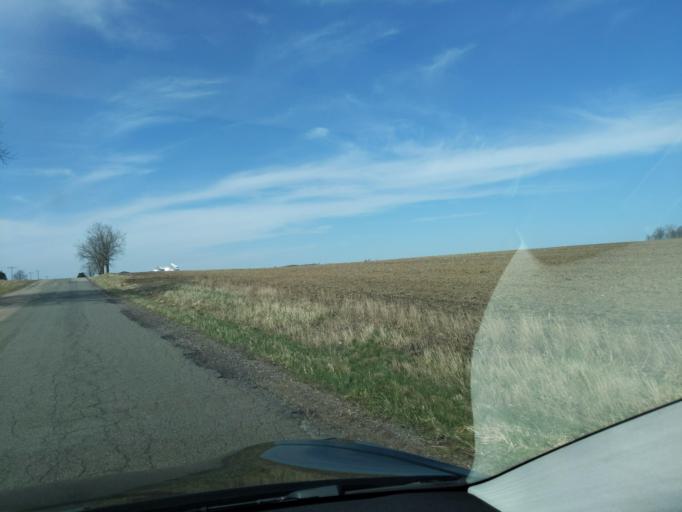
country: US
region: Michigan
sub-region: Ingham County
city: Williamston
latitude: 42.6050
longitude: -84.2991
